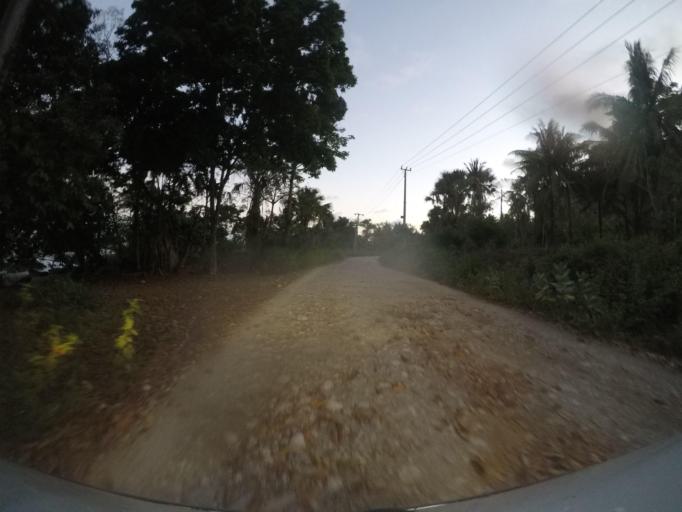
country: TL
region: Viqueque
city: Viqueque
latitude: -8.7952
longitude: 126.6237
